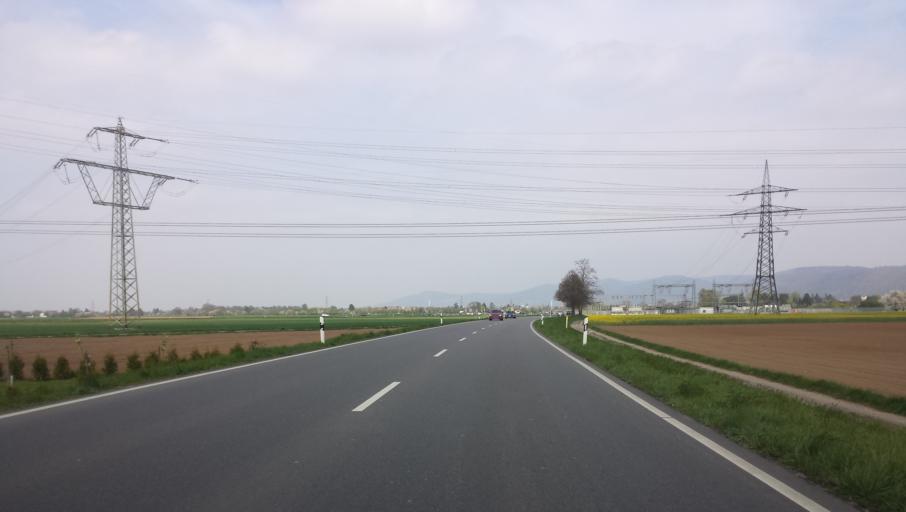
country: DE
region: Baden-Wuerttemberg
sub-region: Karlsruhe Region
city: Sandhausen
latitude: 49.3559
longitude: 8.6609
